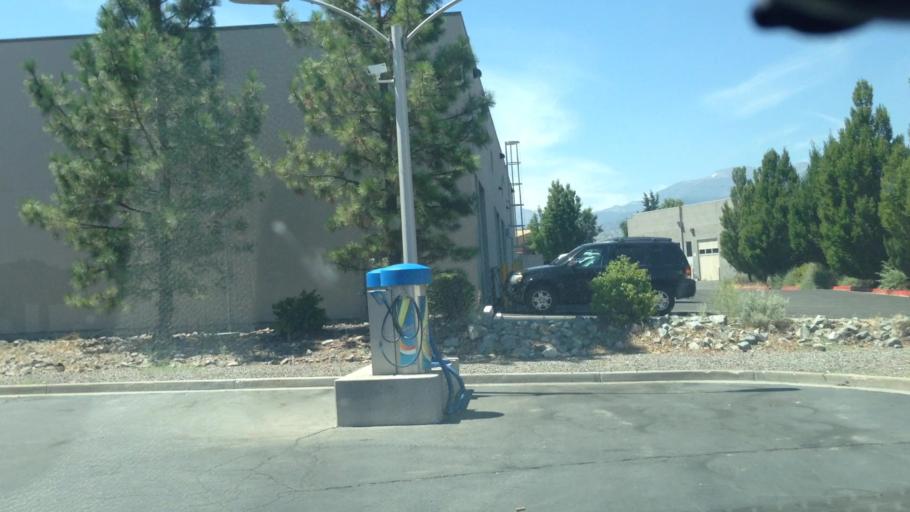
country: US
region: Nevada
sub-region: Washoe County
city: Sparks
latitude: 39.4589
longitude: -119.7753
